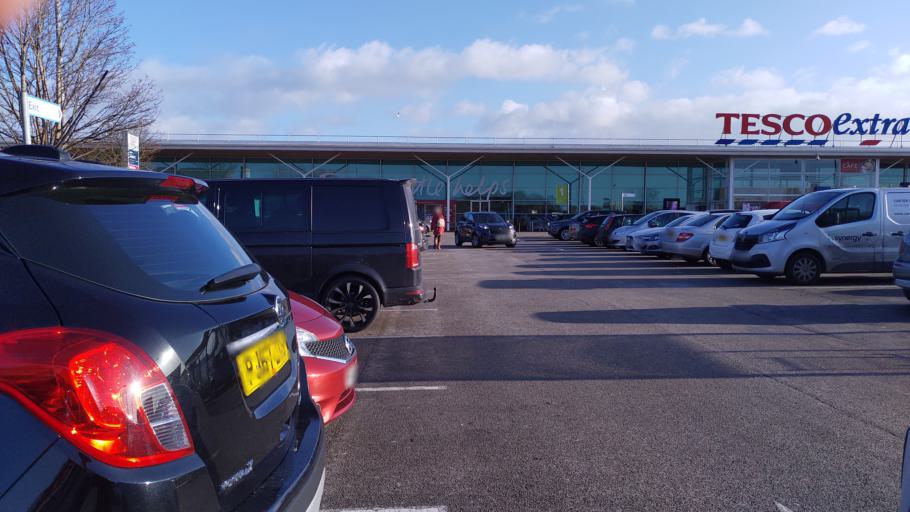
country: GB
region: England
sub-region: Lancashire
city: Leyland
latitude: 53.6902
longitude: -2.6983
